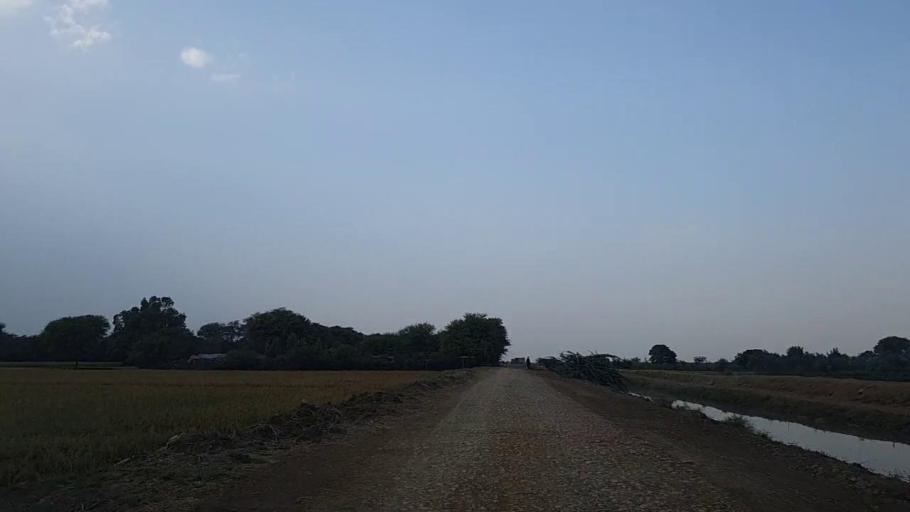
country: PK
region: Sindh
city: Daro Mehar
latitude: 24.7646
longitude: 68.1353
